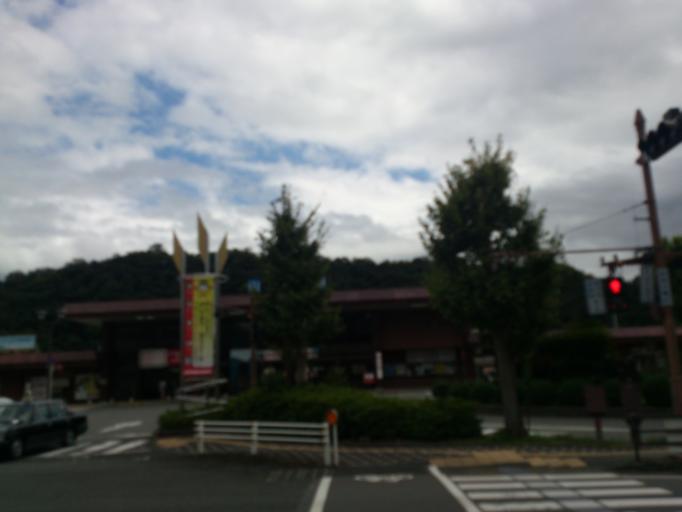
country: JP
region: Yamaguchi
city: Yamaguchi-shi
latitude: 34.1729
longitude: 131.4801
